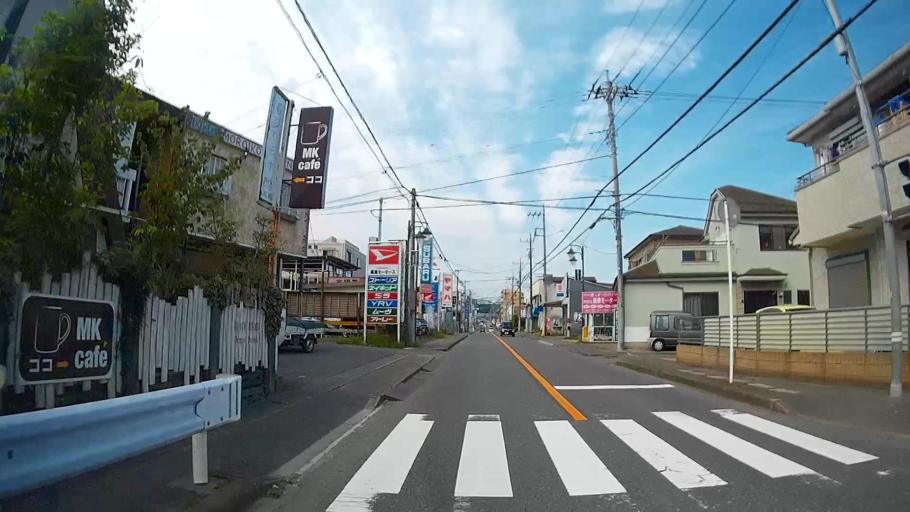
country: JP
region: Saitama
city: Sayama
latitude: 35.8424
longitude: 139.3776
